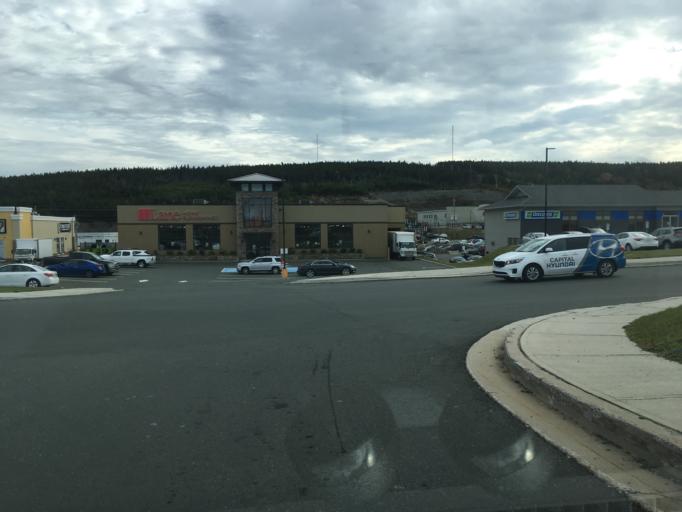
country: CA
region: Newfoundland and Labrador
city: Mount Pearl
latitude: 47.5512
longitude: -52.7812
